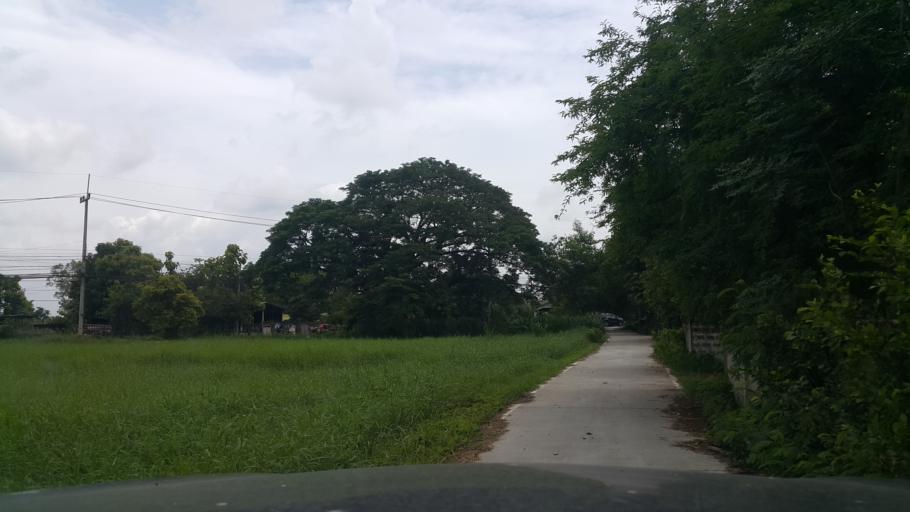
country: TH
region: Lamphun
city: Ban Thi
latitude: 18.6739
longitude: 99.1452
